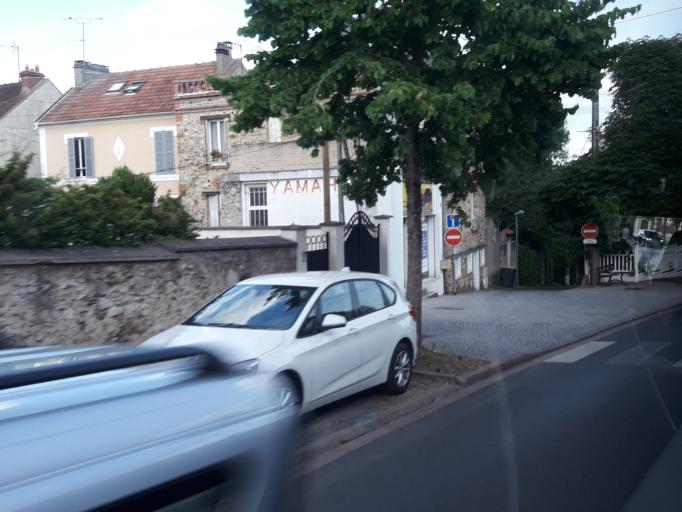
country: FR
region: Ile-de-France
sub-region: Departement de l'Essonne
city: Villemoisson-sur-Orge
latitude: 48.6719
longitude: 2.3306
